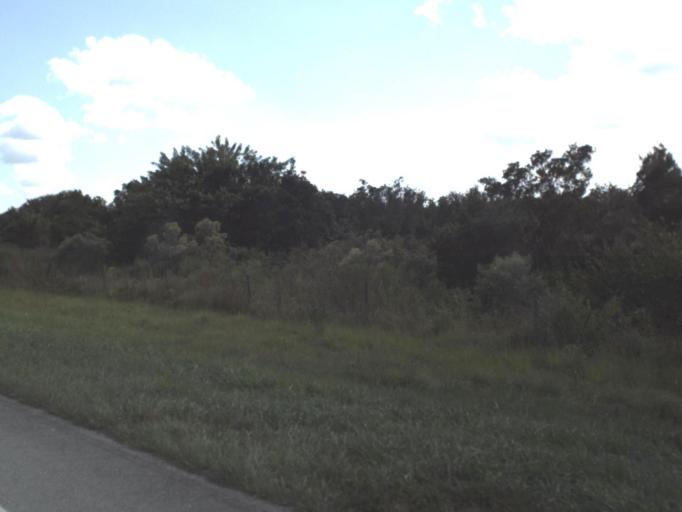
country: US
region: Florida
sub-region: Highlands County
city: Lake Placid
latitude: 27.3768
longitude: -81.0969
